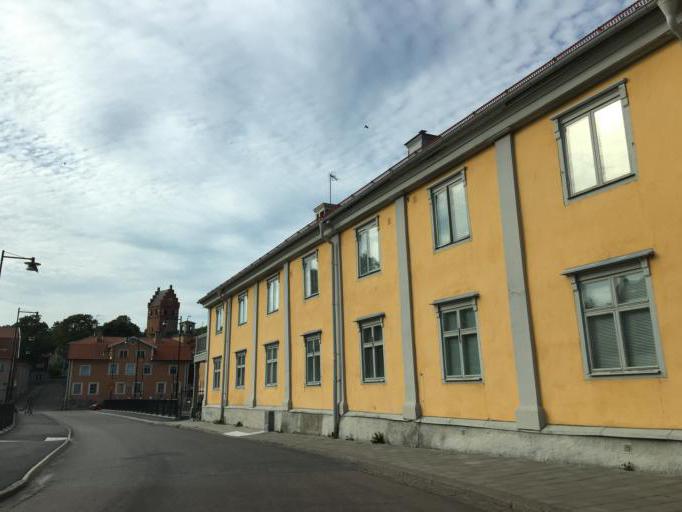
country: SE
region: Soedermanland
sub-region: Eskilstuna Kommun
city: Torshalla
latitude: 59.4206
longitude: 16.4715
